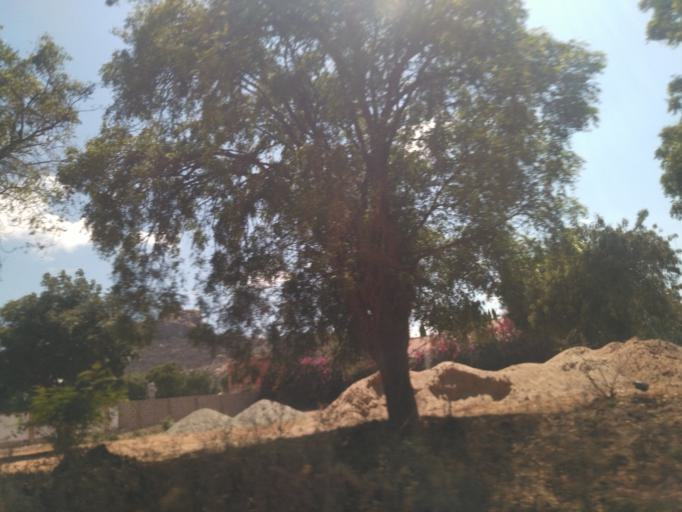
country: TZ
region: Dodoma
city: Dodoma
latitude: -6.1601
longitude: 35.7572
